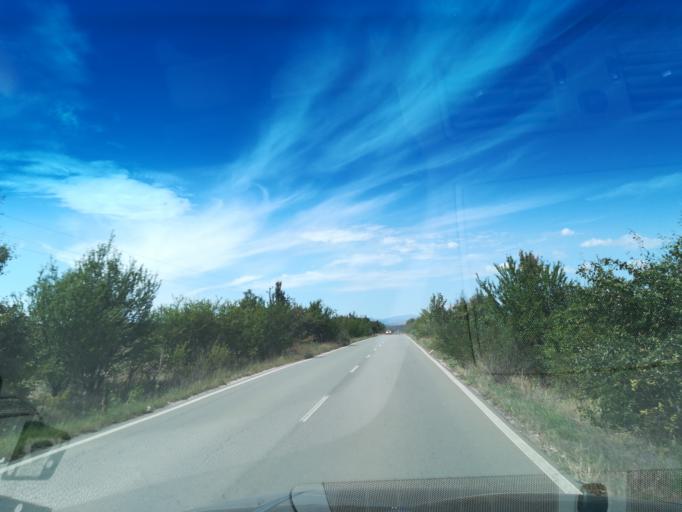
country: BG
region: Plovdiv
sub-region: Obshtina Suedinenie
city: Suedinenie
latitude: 42.4021
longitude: 24.5342
